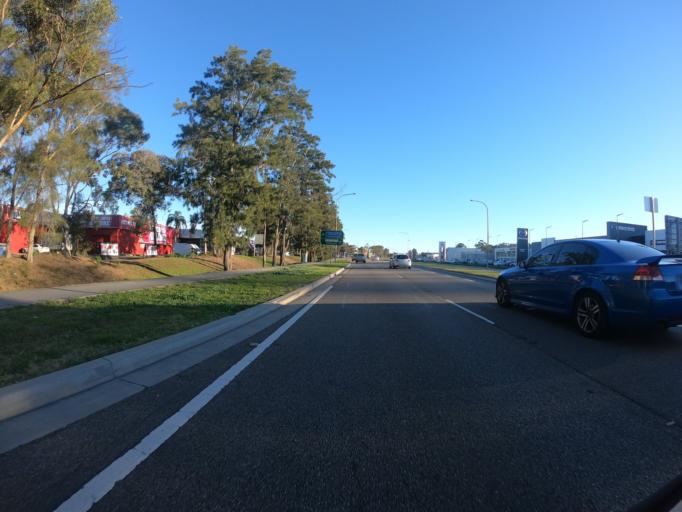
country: AU
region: New South Wales
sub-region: Campbelltown Municipality
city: Leumeah
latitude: -34.0506
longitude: 150.8259
